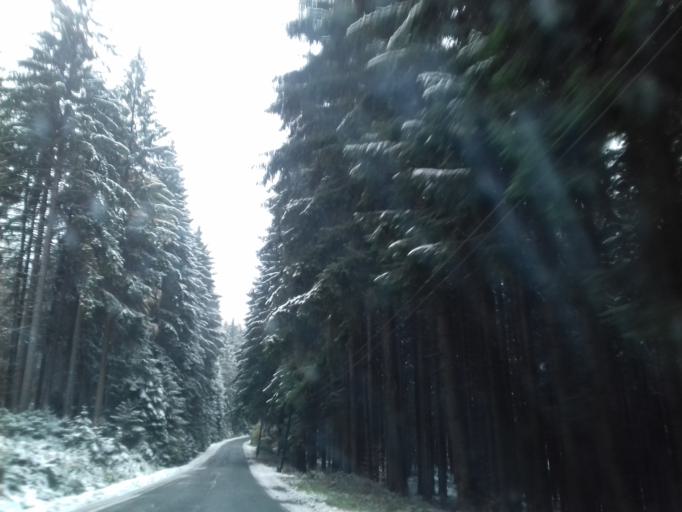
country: CZ
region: Plzensky
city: Postrekov
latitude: 49.4396
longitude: 12.7873
